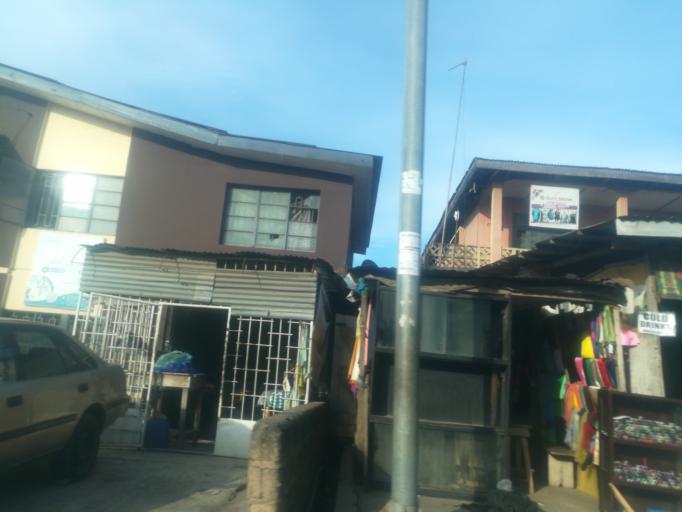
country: NG
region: Oyo
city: Ibadan
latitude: 7.3465
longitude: 3.8837
